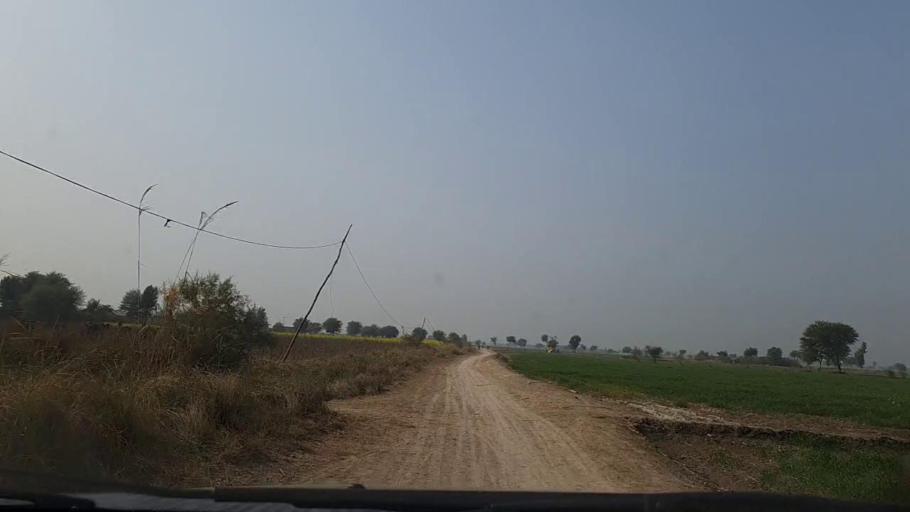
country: PK
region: Sindh
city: Sanghar
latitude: 26.0345
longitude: 68.9976
